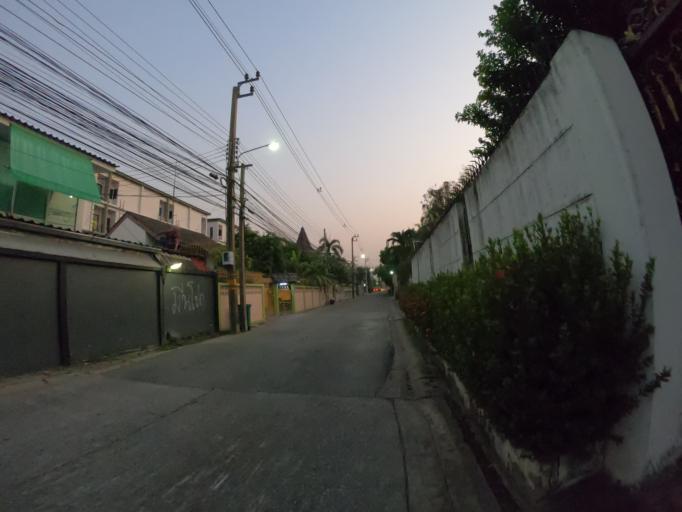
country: TH
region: Bangkok
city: Lat Phrao
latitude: 13.8274
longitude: 100.6208
